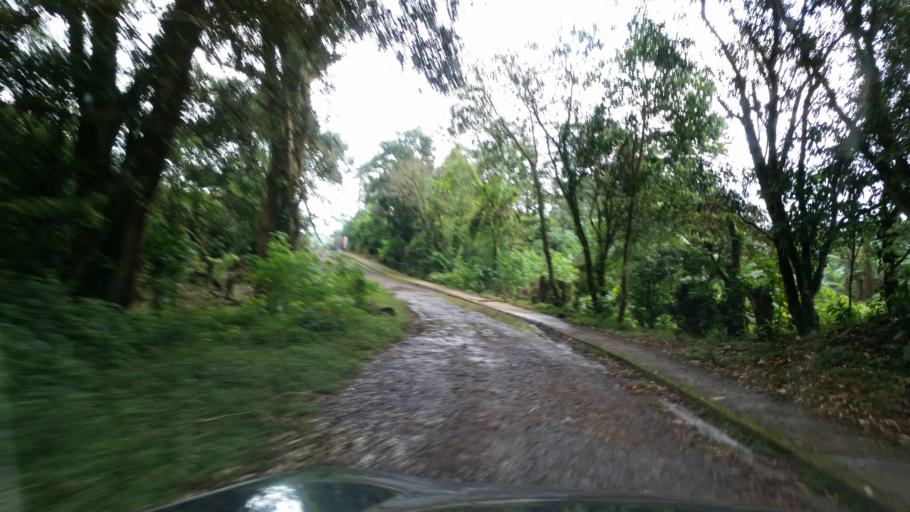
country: NI
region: Jinotega
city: San Jose de Bocay
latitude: 13.2788
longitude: -85.7171
